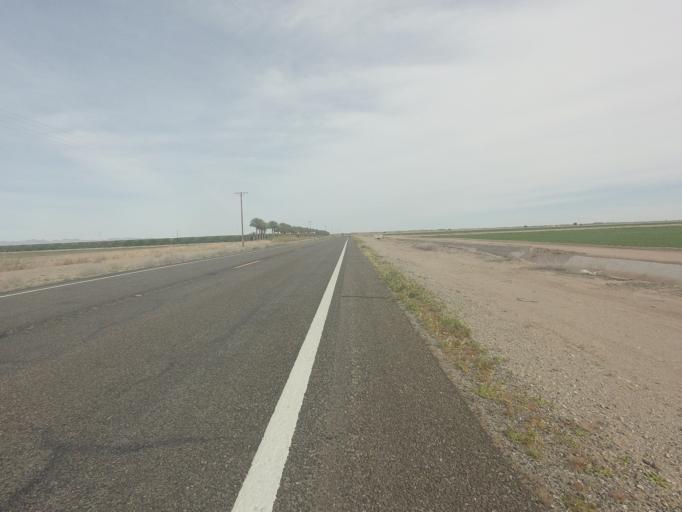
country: US
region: California
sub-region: Imperial County
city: Holtville
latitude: 32.9747
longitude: -115.3174
